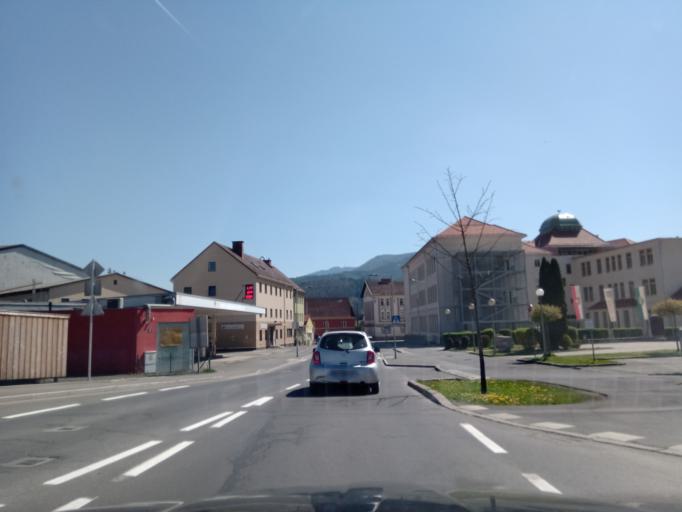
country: AT
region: Styria
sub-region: Politischer Bezirk Leoben
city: Leoben
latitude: 47.3746
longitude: 15.0817
